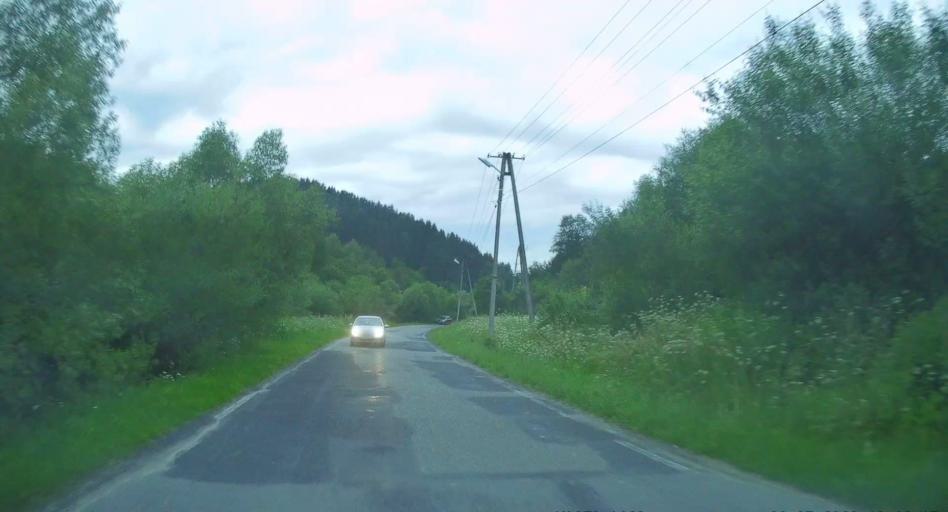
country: PL
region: Lesser Poland Voivodeship
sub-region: Powiat nowosadecki
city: Muszyna
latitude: 49.3703
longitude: 20.9236
